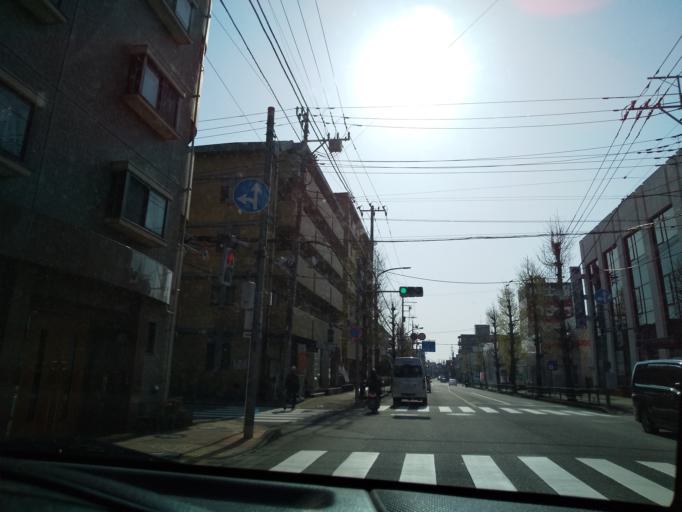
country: JP
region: Tokyo
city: Hino
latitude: 35.7073
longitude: 139.3764
